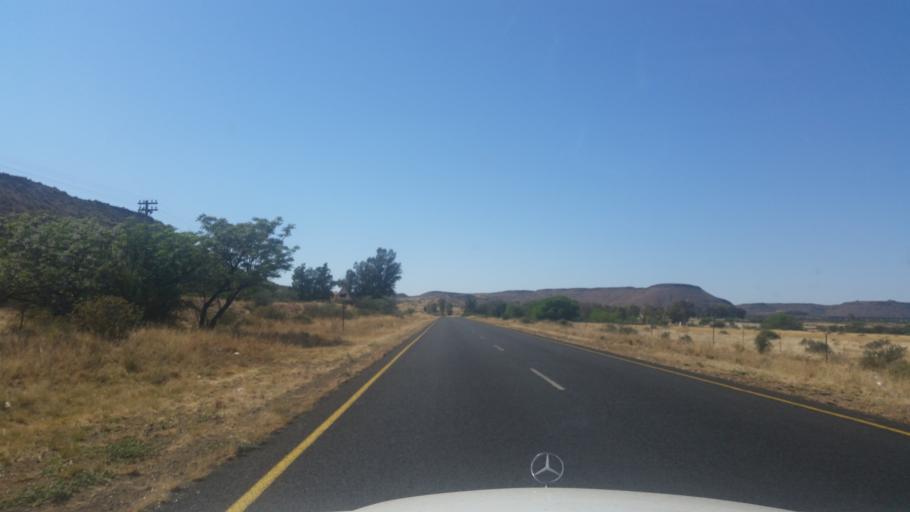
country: ZA
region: Orange Free State
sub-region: Xhariep District Municipality
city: Trompsburg
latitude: -30.4952
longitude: 25.9994
